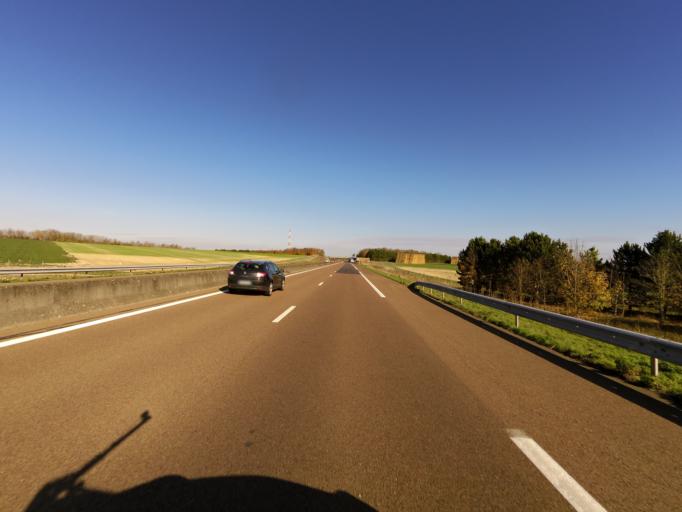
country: FR
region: Champagne-Ardenne
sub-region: Departement de la Marne
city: Compertrix
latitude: 48.8742
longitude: 4.2892
